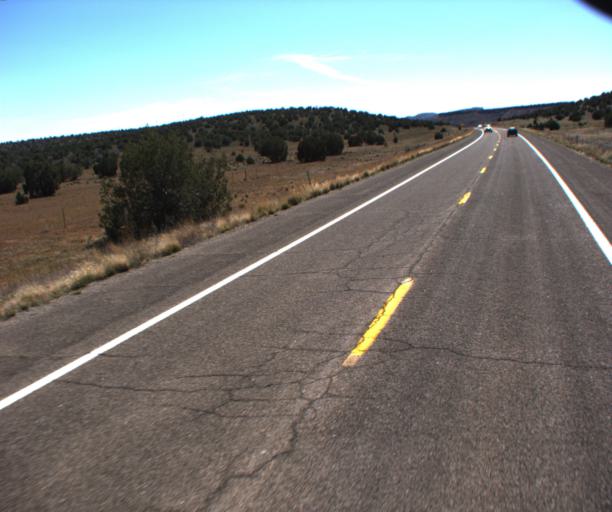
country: US
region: Arizona
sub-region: Mohave County
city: Peach Springs
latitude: 35.4519
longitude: -113.6311
